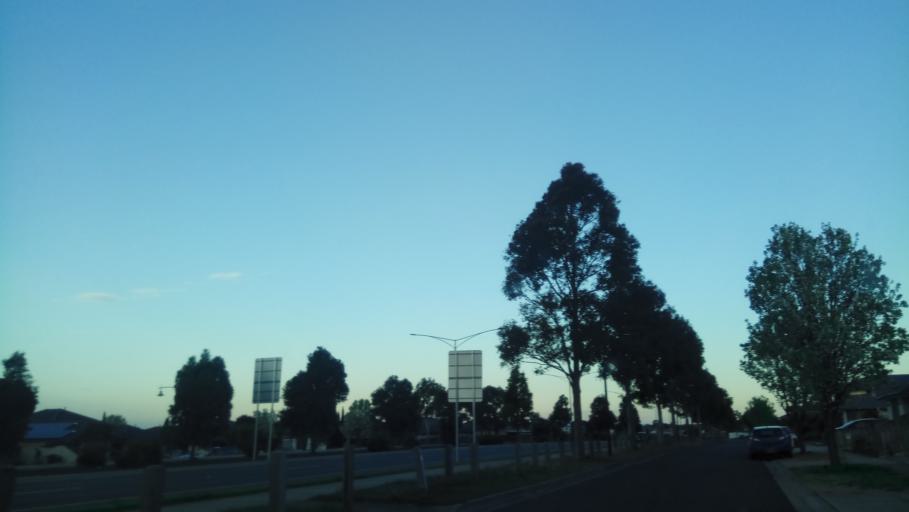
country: AU
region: Victoria
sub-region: Wyndham
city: Point Cook
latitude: -37.8996
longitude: 144.7460
